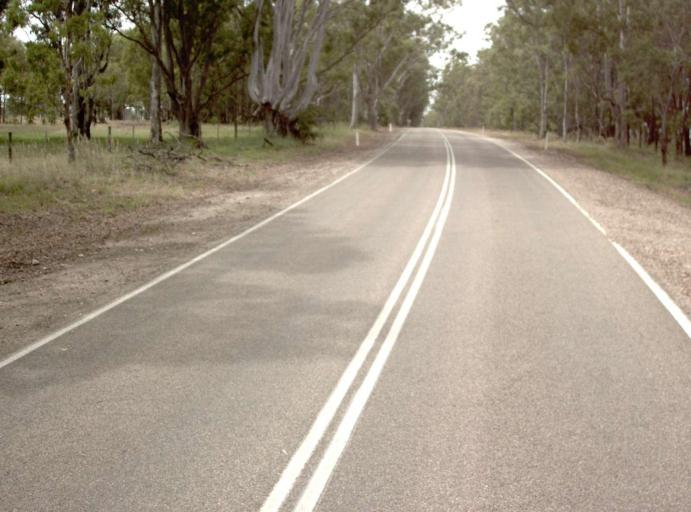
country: AU
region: Victoria
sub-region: Wellington
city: Sale
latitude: -37.8864
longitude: 147.0645
